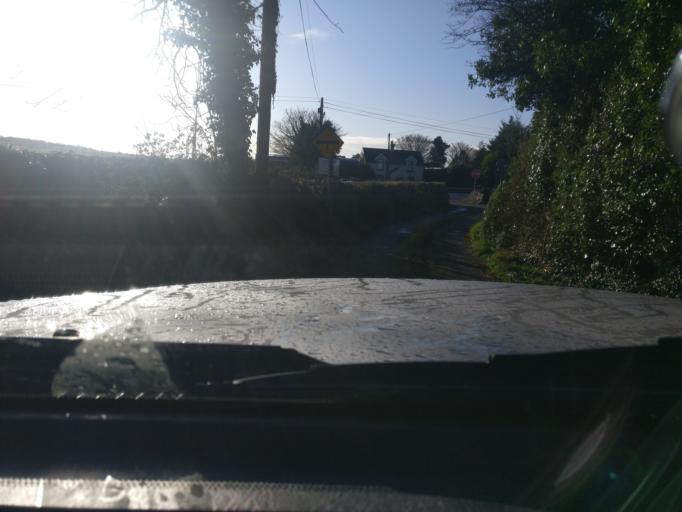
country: IE
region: Connaught
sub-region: County Galway
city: Loughrea
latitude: 53.2114
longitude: -8.5108
